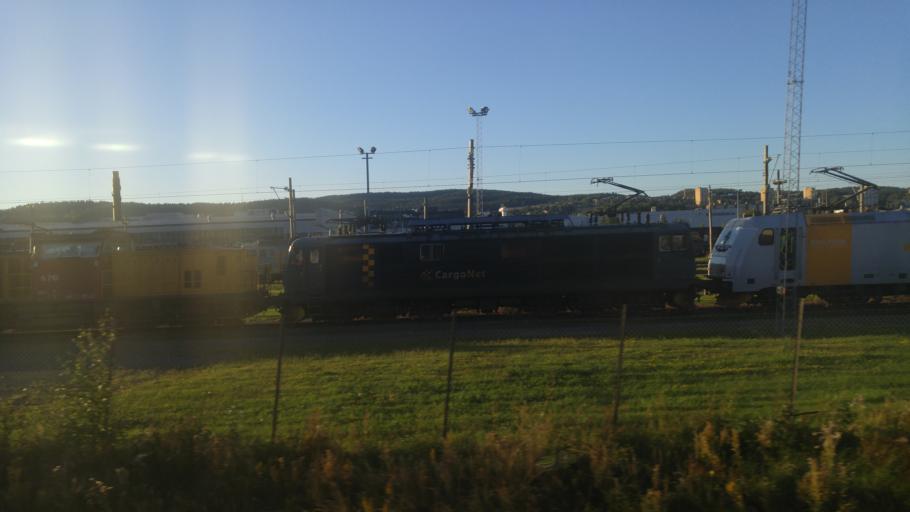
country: NO
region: Akershus
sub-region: Lorenskog
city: Kjenn
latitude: 59.9420
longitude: 10.8648
